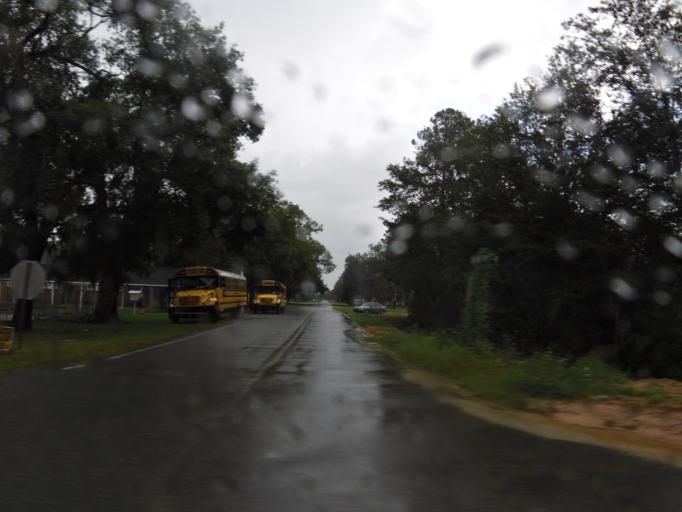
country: US
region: Florida
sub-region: Nassau County
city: Hilliard
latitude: 30.5244
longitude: -82.0392
